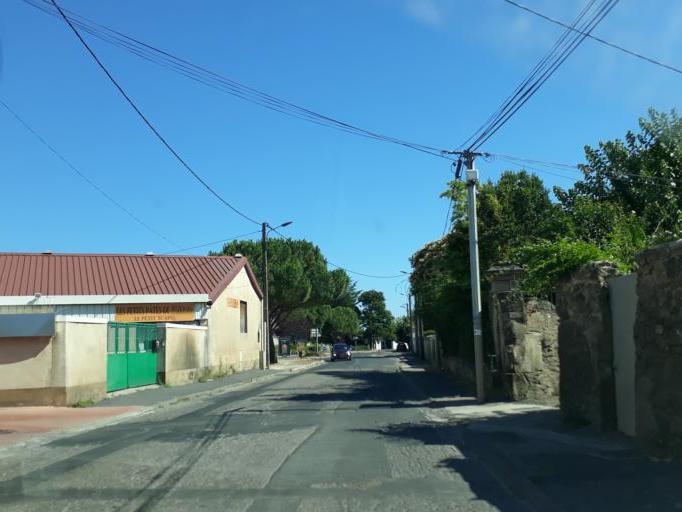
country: FR
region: Languedoc-Roussillon
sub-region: Departement de l'Herault
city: Pezenas
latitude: 43.4544
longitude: 3.4266
